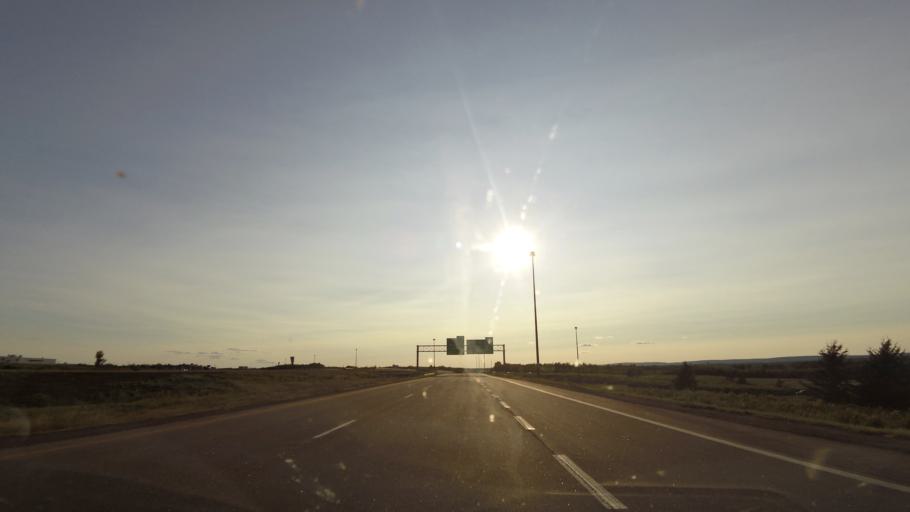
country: CA
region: New Brunswick
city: Dieppe
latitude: 46.1285
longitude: -64.6774
